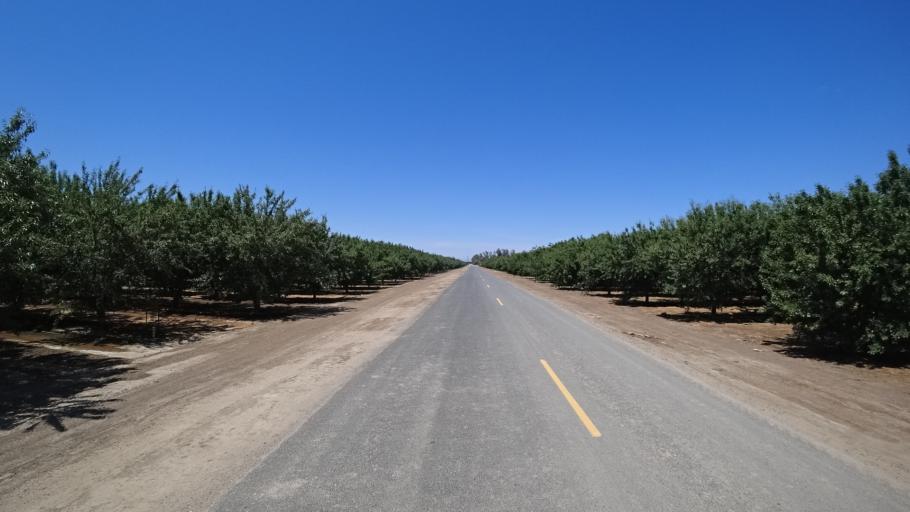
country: US
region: California
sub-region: Kings County
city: Lemoore
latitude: 36.3571
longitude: -119.8025
